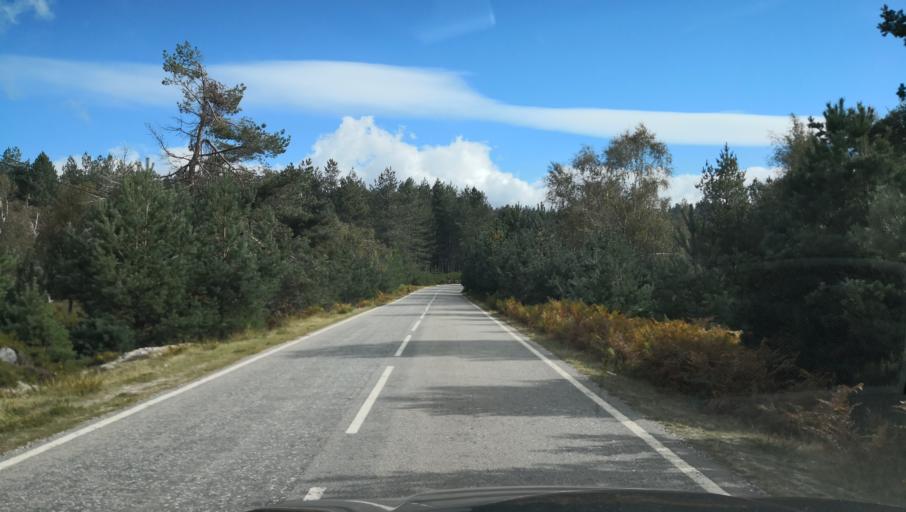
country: PT
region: Vila Real
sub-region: Vila Real
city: Vila Real
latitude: 41.3562
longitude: -7.7935
